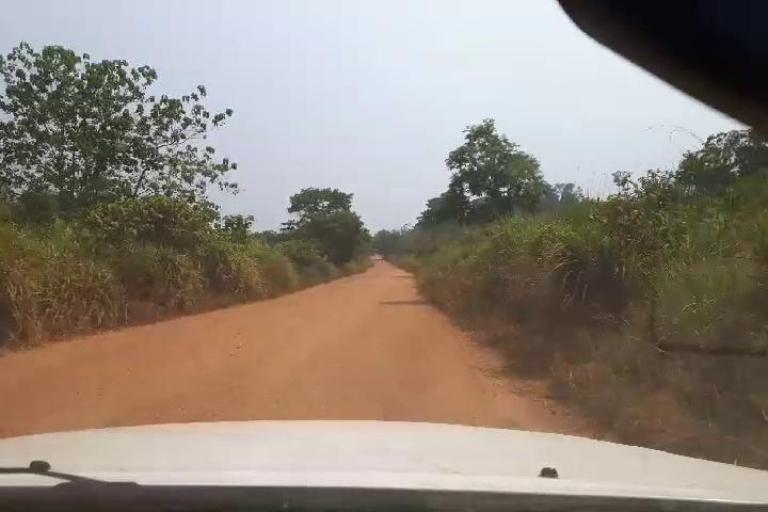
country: SL
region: Northern Province
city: Bumbuna
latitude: 9.0177
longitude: -11.7651
